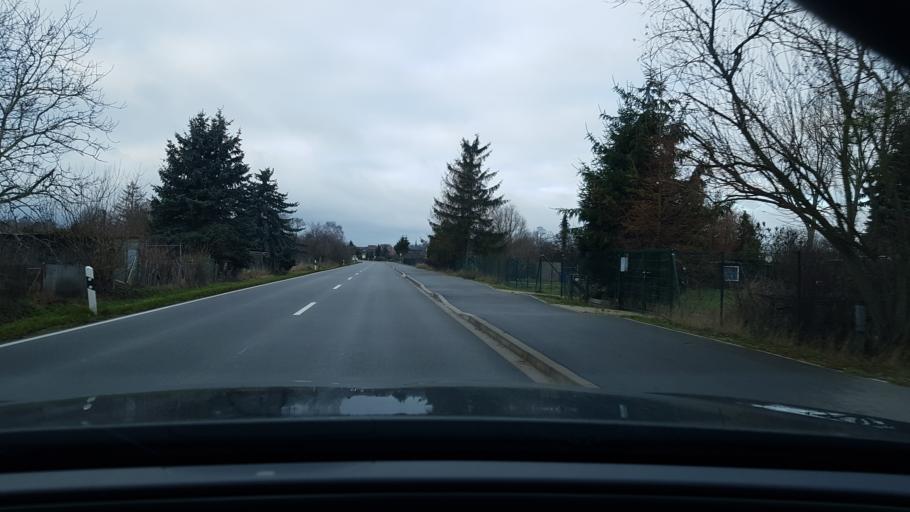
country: DE
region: Saxony-Anhalt
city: Oebisfelde
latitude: 52.4252
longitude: 10.9992
